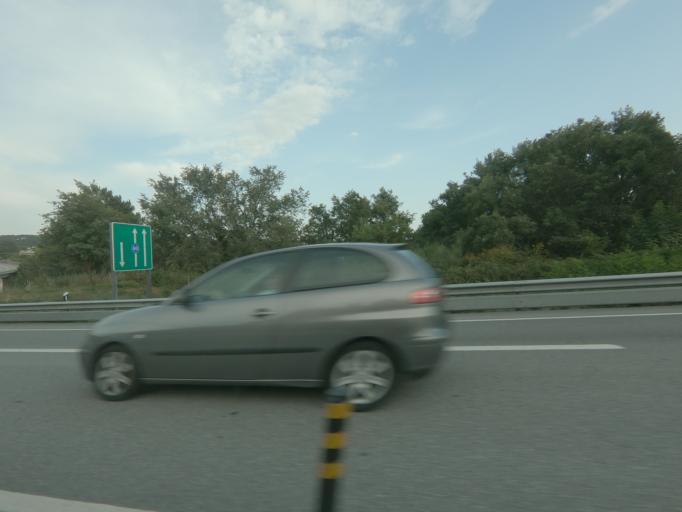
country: PT
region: Vila Real
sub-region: Vila Real
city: Vila Real
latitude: 41.3167
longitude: -7.7265
